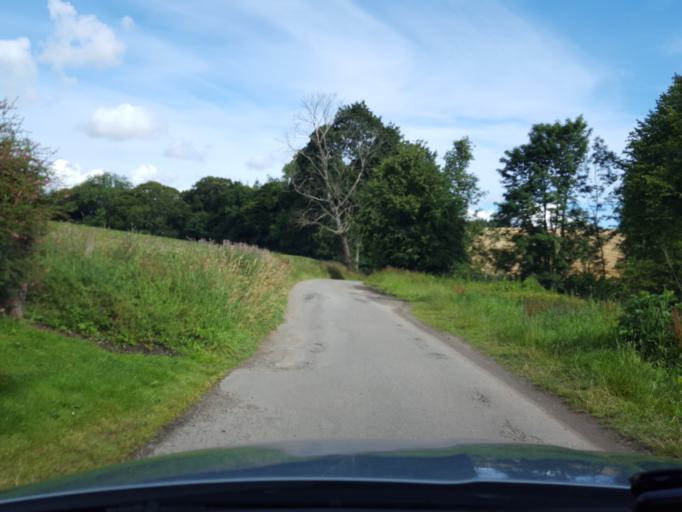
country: GB
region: Scotland
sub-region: Moray
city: Rothes
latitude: 57.4749
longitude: -3.1970
